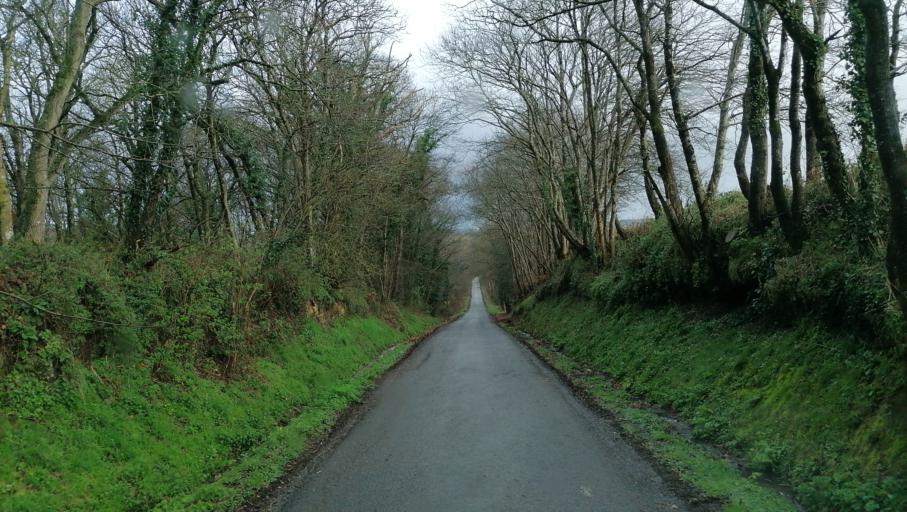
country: FR
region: Brittany
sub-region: Departement des Cotes-d'Armor
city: Plouagat
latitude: 48.4871
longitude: -2.9622
